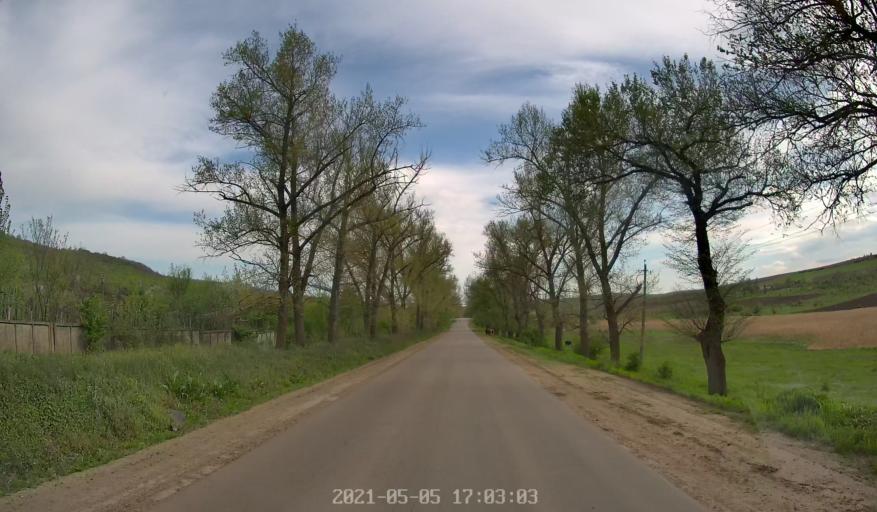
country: MD
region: Chisinau
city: Vadul lui Voda
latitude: 47.0548
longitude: 29.1327
